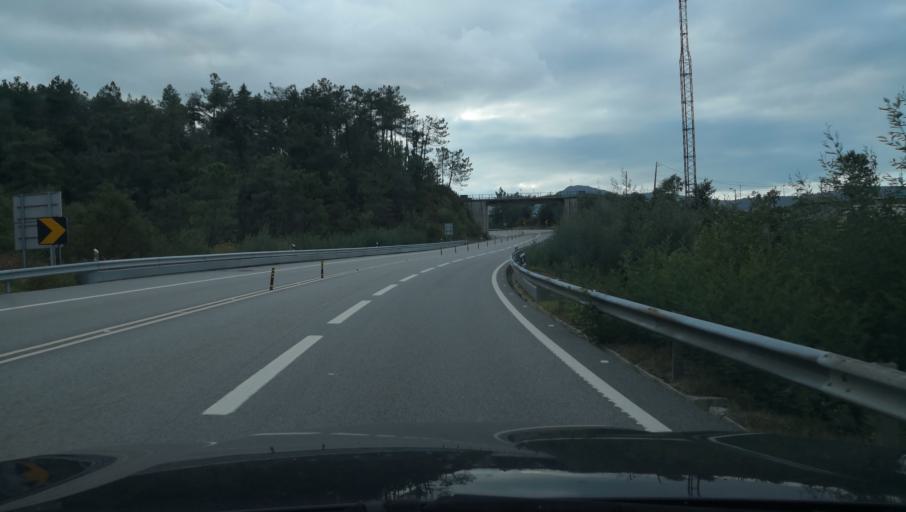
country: PT
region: Vila Real
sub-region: Santa Marta de Penaguiao
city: Santa Marta de Penaguiao
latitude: 41.2805
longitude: -7.8721
